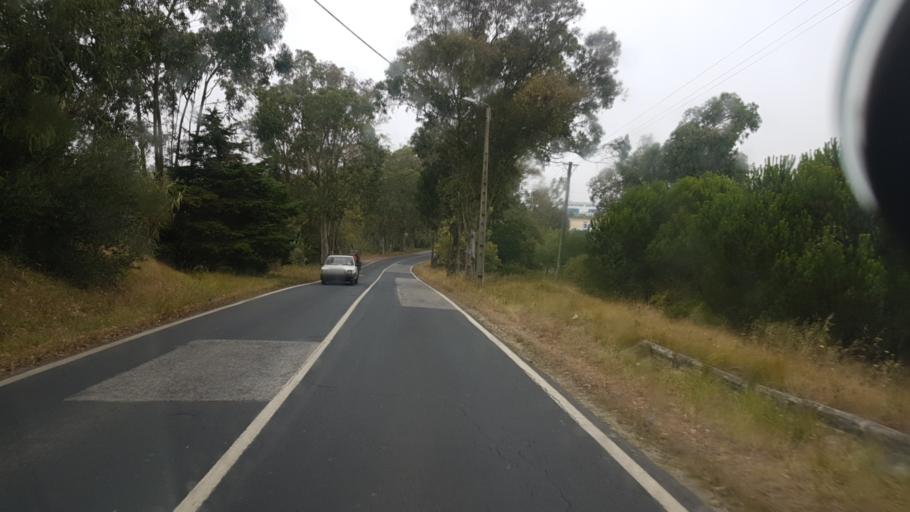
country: PT
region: Lisbon
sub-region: Sintra
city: Sintra
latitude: 38.8197
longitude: -9.3671
